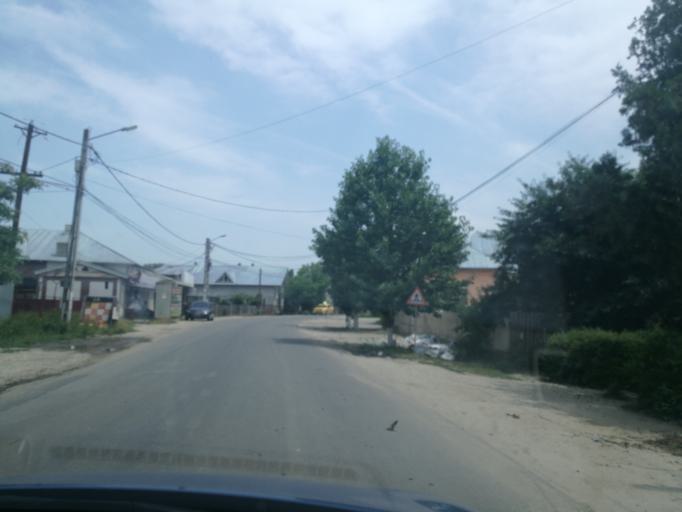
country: RO
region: Ilfov
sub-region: Comuna Vidra
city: Vidra
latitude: 44.2645
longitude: 26.1538
